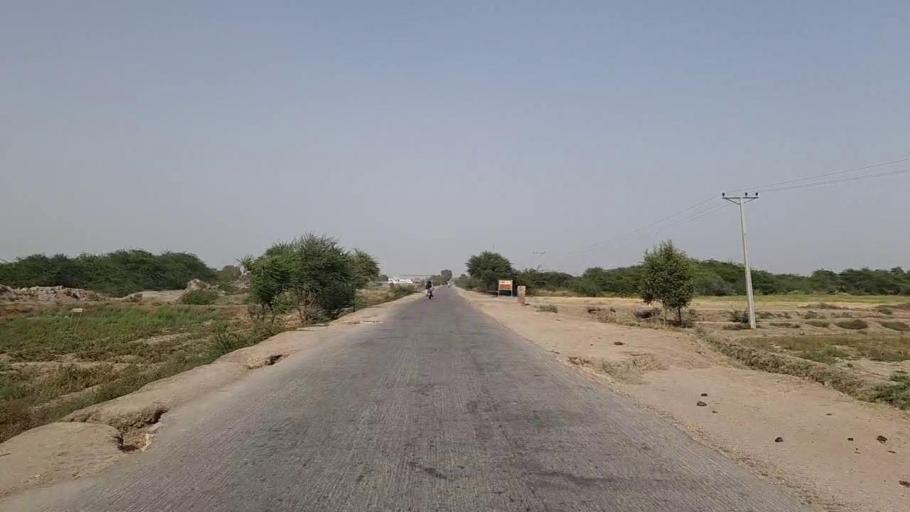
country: PK
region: Sindh
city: Tando Bago
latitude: 24.9185
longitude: 69.1012
